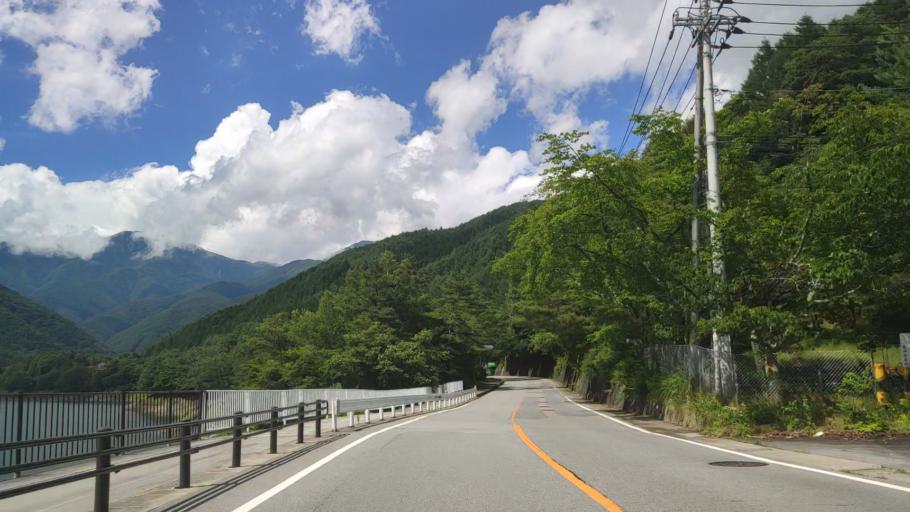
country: JP
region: Yamanashi
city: Enzan
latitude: 35.8424
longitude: 138.7637
